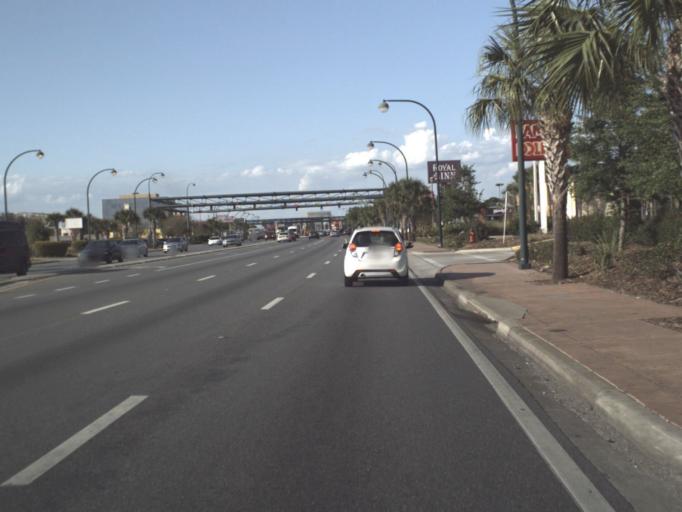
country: US
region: Florida
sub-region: Orange County
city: Sky Lake
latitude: 28.4616
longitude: -81.3975
